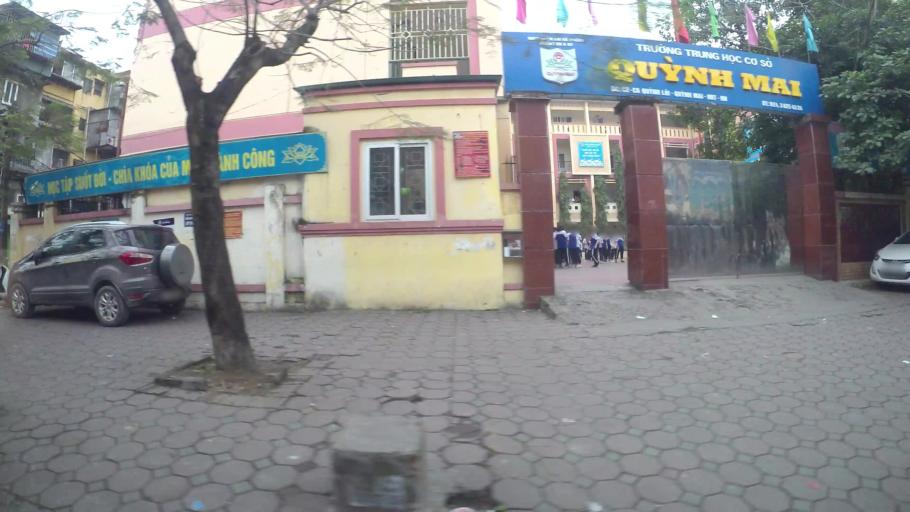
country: VN
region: Ha Noi
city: Hai BaTrung
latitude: 21.0017
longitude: 105.8597
